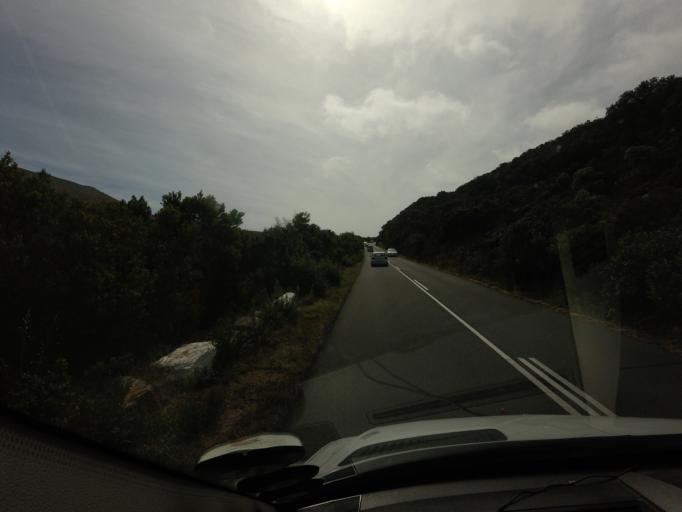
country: ZA
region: Western Cape
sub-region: City of Cape Town
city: Retreat
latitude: -34.2613
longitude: 18.4643
